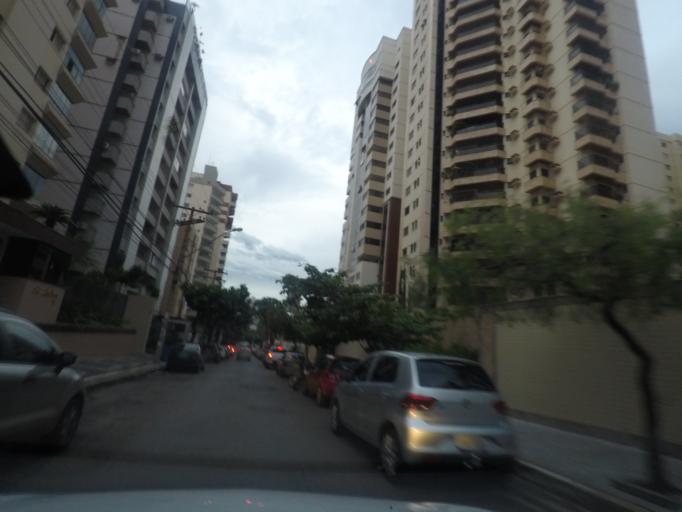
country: BR
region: Goias
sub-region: Goiania
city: Goiania
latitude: -16.7122
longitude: -49.2682
